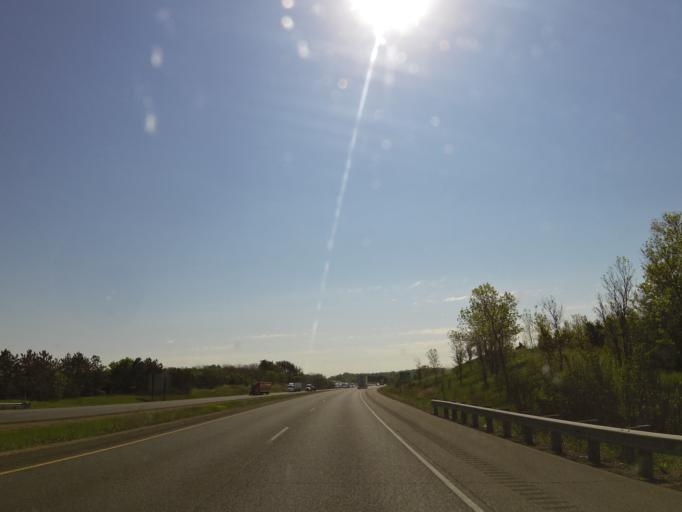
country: US
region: Wisconsin
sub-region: Saint Croix County
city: Hudson
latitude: 44.9649
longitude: -92.6582
